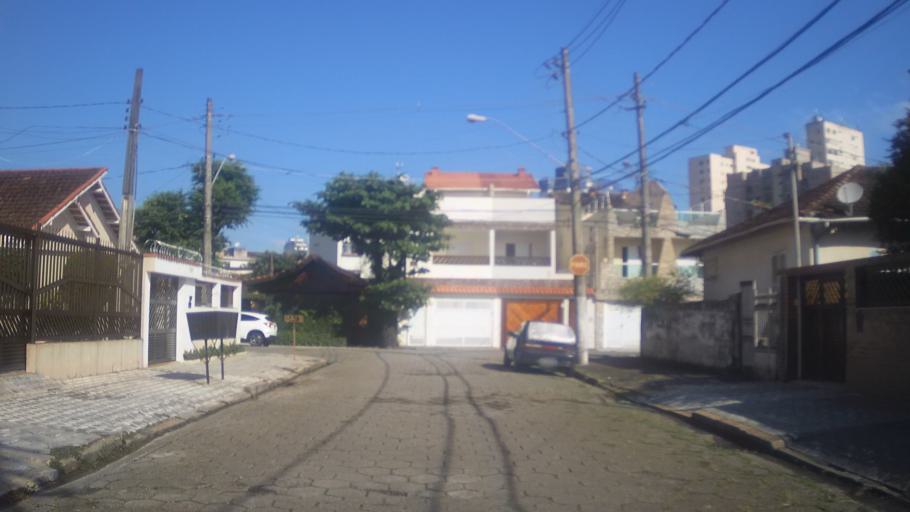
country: BR
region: Sao Paulo
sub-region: Sao Vicente
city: Sao Vicente
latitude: -23.9640
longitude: -46.3797
